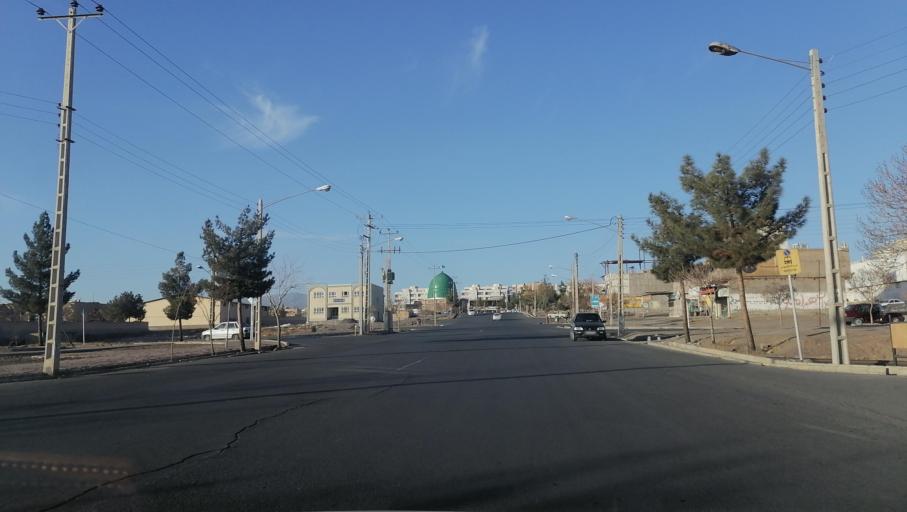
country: IR
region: Razavi Khorasan
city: Sabzevar
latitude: 36.2823
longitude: 57.6752
